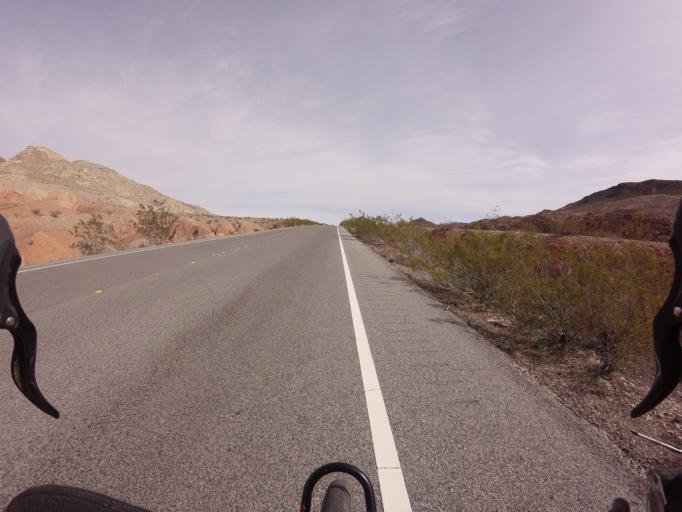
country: US
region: Nevada
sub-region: Clark County
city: Boulder City
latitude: 36.1957
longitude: -114.7072
